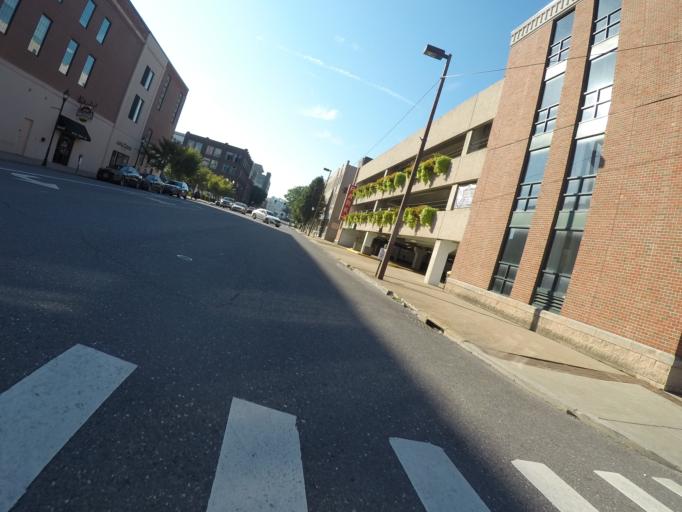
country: US
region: West Virginia
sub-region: Cabell County
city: Huntington
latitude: 38.4215
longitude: -82.4459
